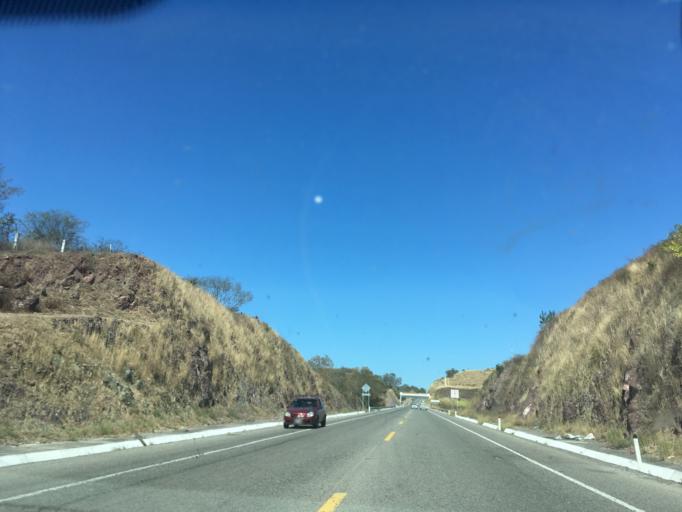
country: MX
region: Guerrero
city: La Union
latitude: 18.0223
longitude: -101.9550
